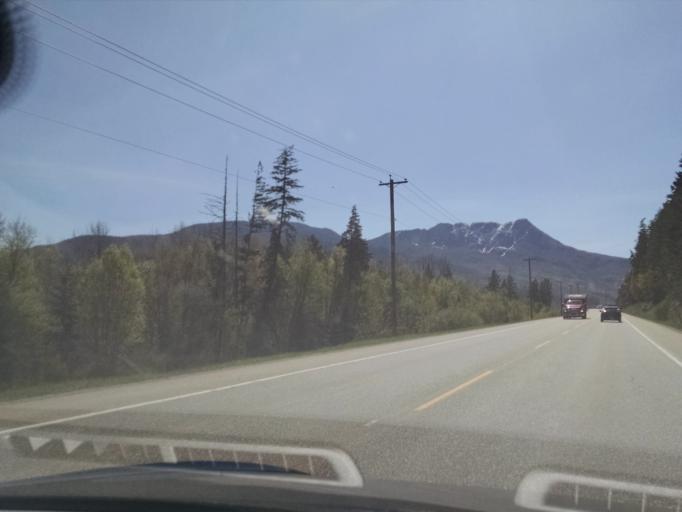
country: CA
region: British Columbia
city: Salmon Arm
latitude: 50.7190
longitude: -119.3178
